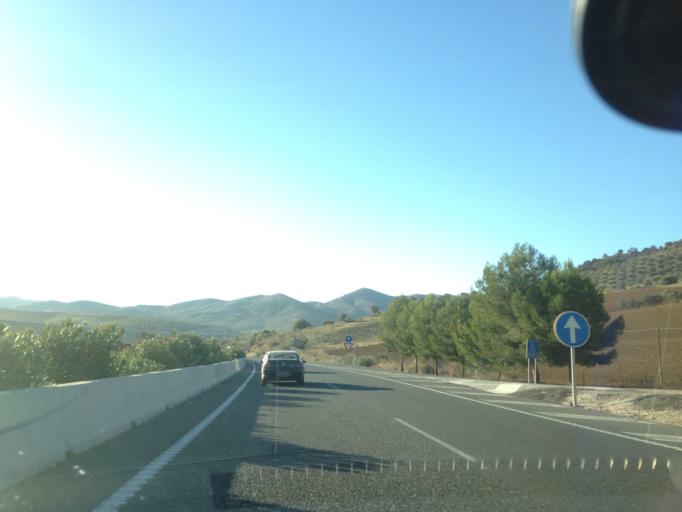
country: ES
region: Andalusia
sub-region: Provincia de Malaga
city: Casabermeja
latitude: 36.9231
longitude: -4.4475
